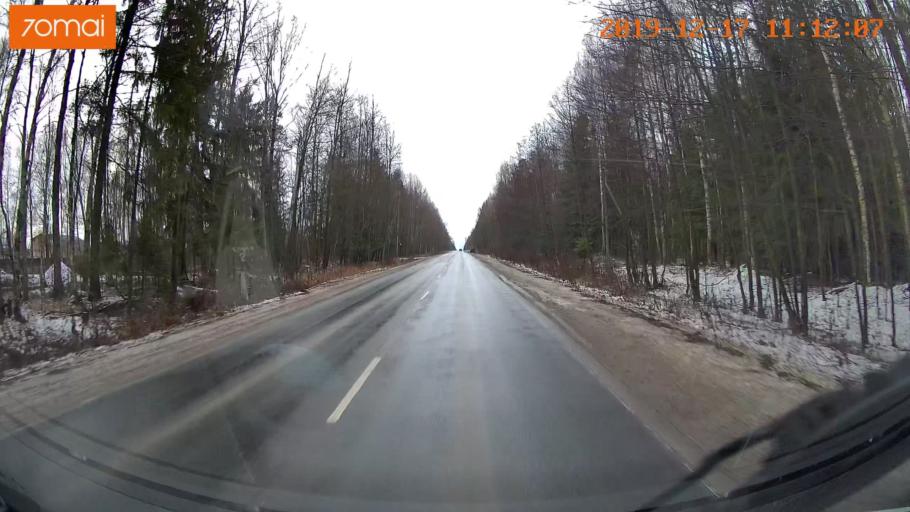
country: RU
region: Vladimir
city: Gus'-Khrustal'nyy
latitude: 55.5799
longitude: 40.6316
